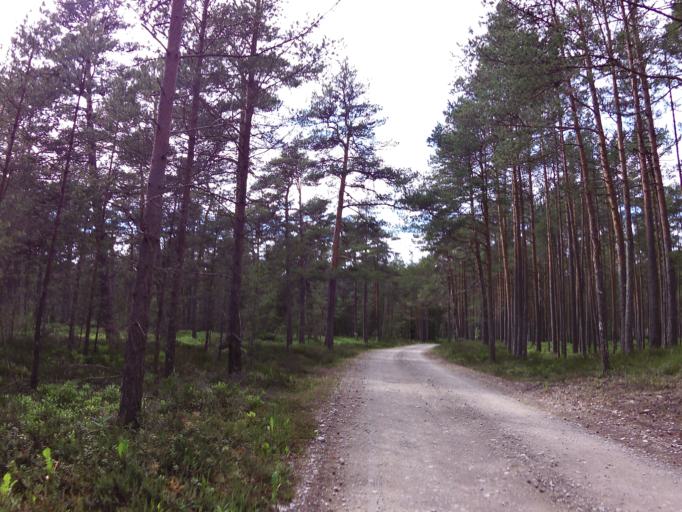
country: EE
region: Laeaene
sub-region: Ridala Parish
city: Uuemoisa
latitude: 59.2233
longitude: 23.6986
